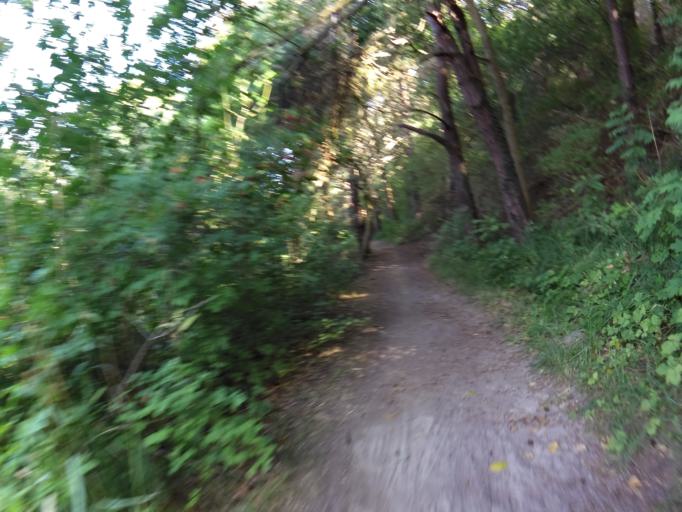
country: DE
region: Mecklenburg-Vorpommern
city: Loddin
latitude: 53.9668
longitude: 14.0434
